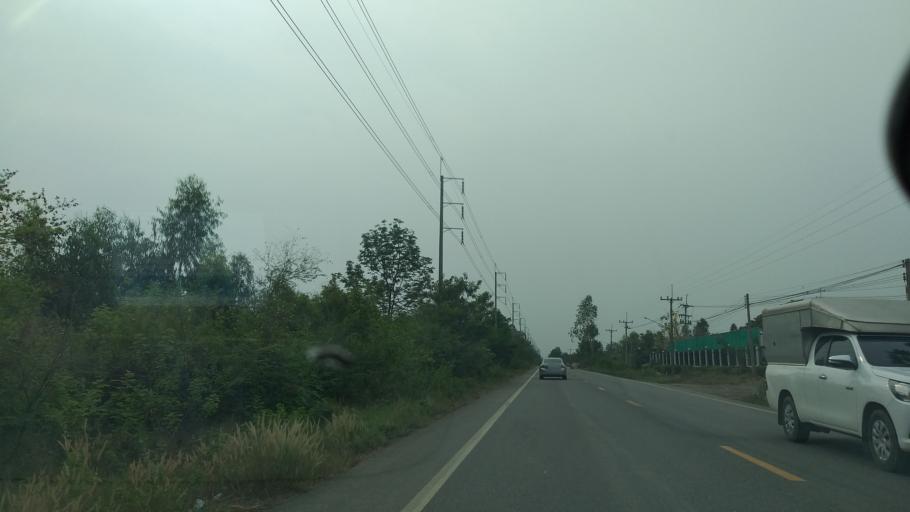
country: TH
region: Chachoengsao
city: Plaeng Yao
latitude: 13.5809
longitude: 101.2309
